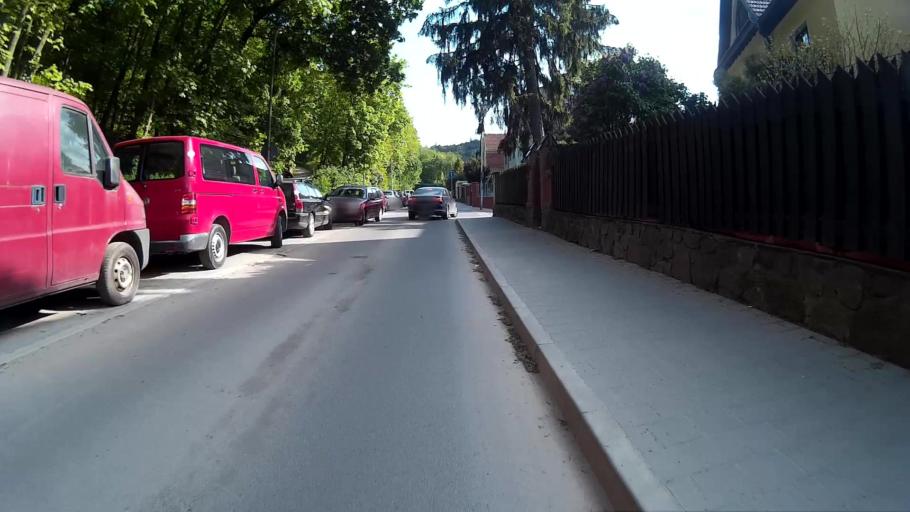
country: CZ
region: South Moravian
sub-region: Mesto Brno
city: Brno
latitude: 49.2103
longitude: 16.5782
